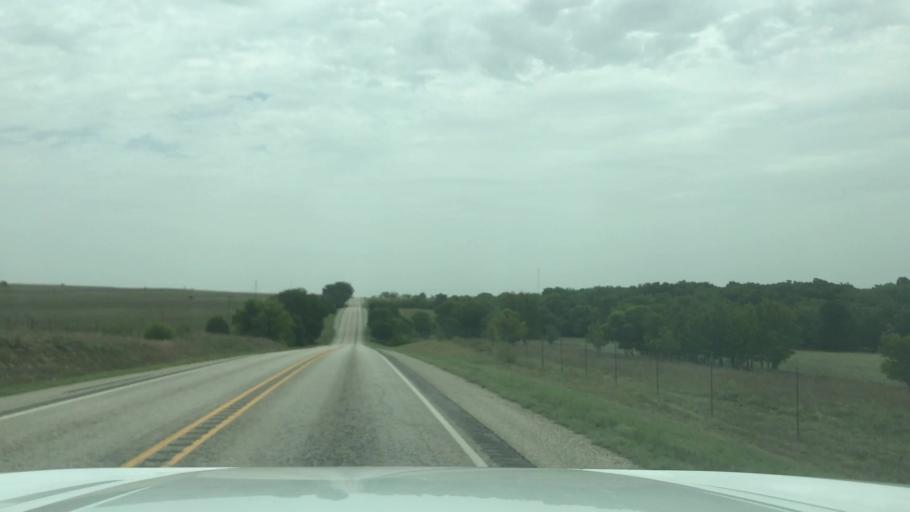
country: US
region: Texas
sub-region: Erath County
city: Dublin
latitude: 32.0557
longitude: -98.1809
